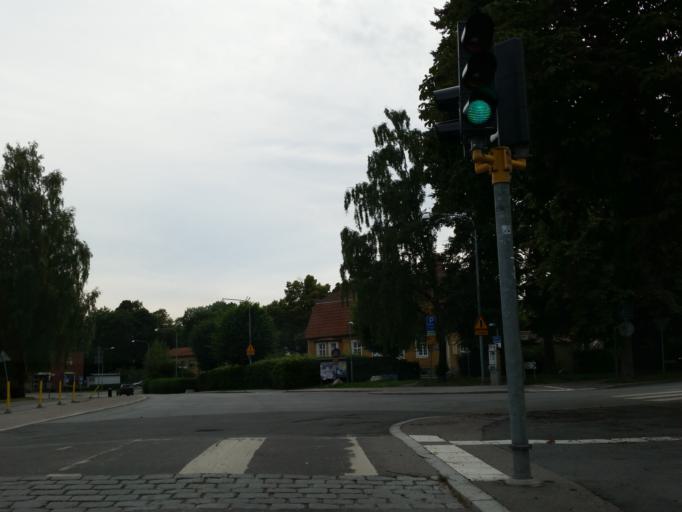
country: SE
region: Stockholm
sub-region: Solna Kommun
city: Rasunda
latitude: 59.3629
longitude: 17.9897
